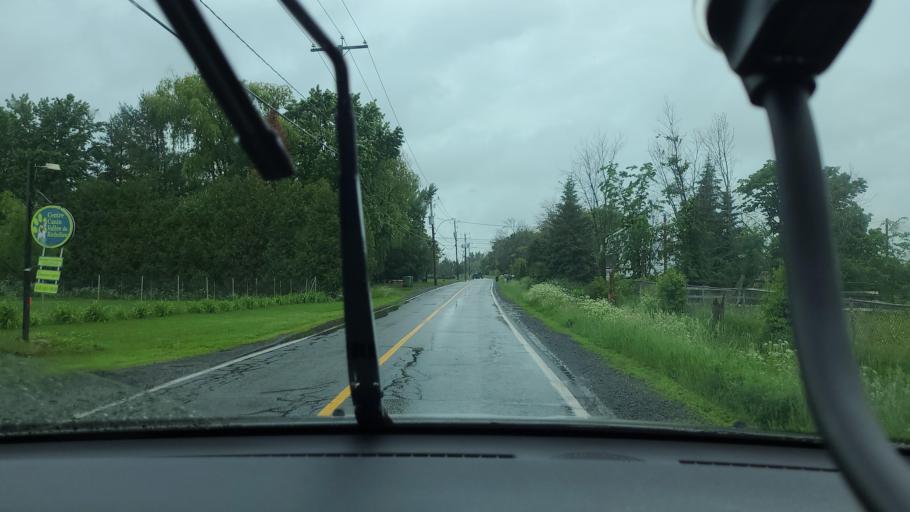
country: CA
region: Quebec
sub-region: Monteregie
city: Saint-Basile-le-Grand
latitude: 45.5459
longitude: -73.2721
